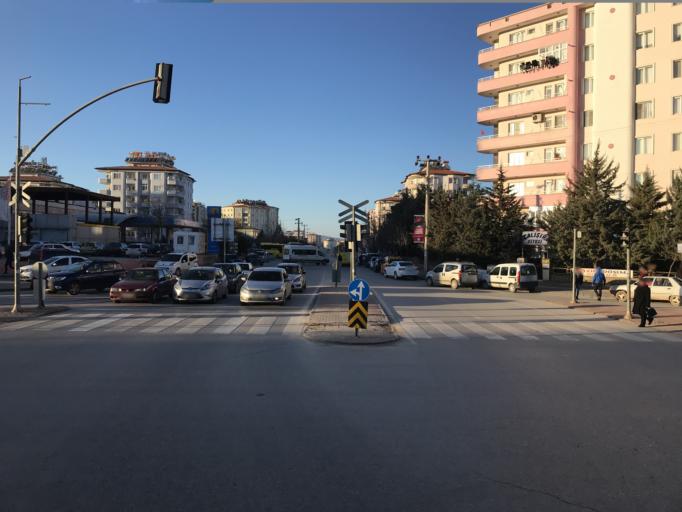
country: TR
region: Gaziantep
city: Sahinbey
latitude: 37.0154
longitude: 37.3526
